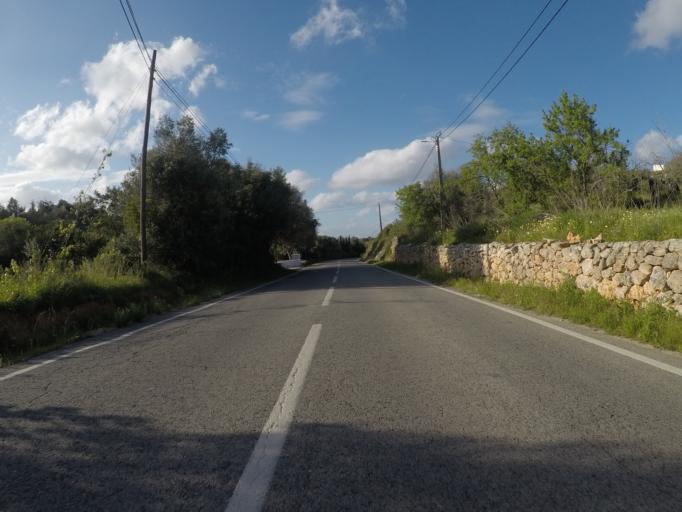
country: PT
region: Faro
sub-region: Lagoa
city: Carvoeiro
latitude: 37.1071
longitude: -8.4461
